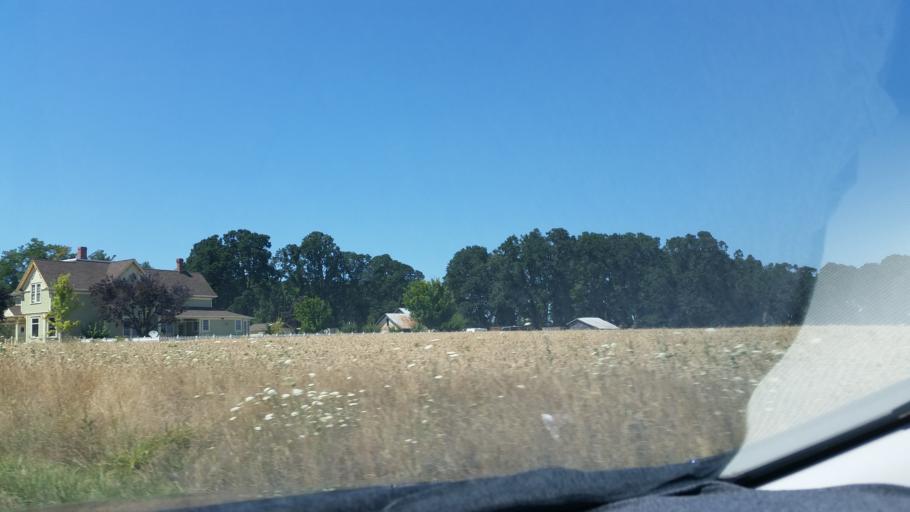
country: US
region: Oregon
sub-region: Clackamas County
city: Wilsonville
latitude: 45.2596
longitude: -122.8004
